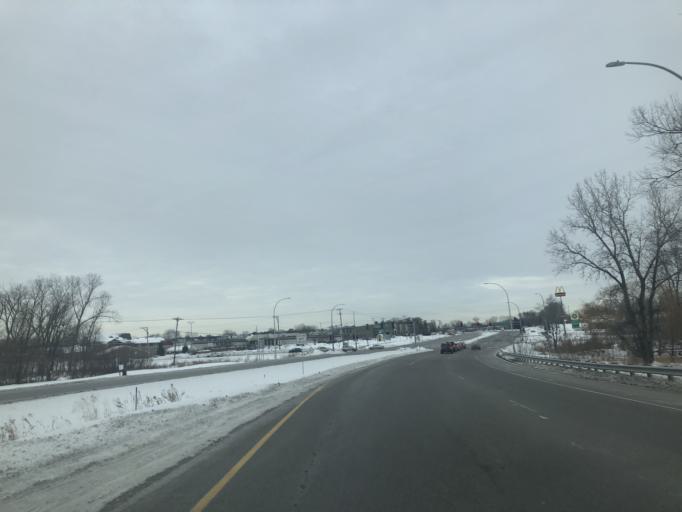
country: US
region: Minnesota
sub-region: Ramsey County
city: Mounds View
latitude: 45.0935
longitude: -93.1912
